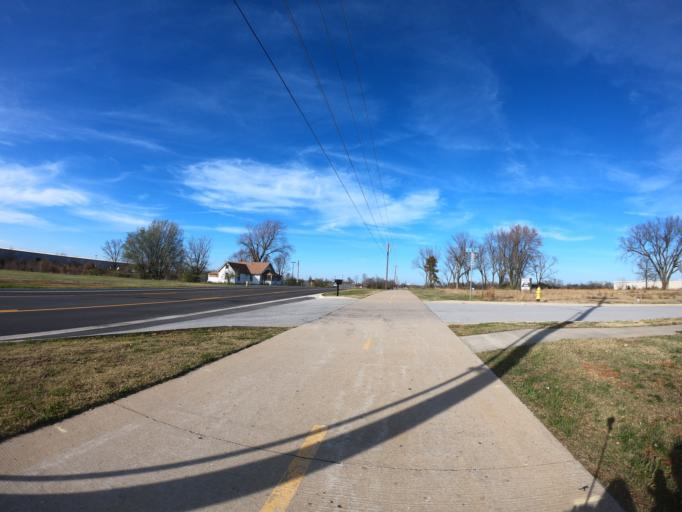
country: US
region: Arkansas
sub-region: Benton County
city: Lowell
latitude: 36.2589
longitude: -94.1547
